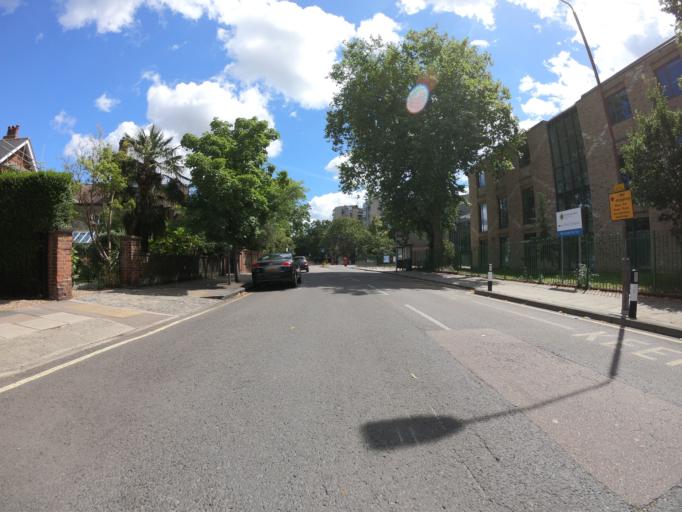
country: GB
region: England
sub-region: Greater London
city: Blackheath
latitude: 51.4794
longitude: 0.0097
